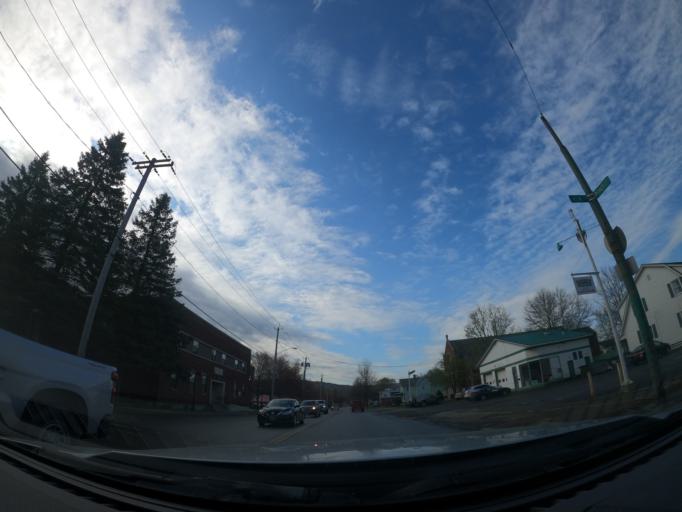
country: US
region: New York
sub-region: Cortland County
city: Cortland
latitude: 42.6023
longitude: -76.1670
